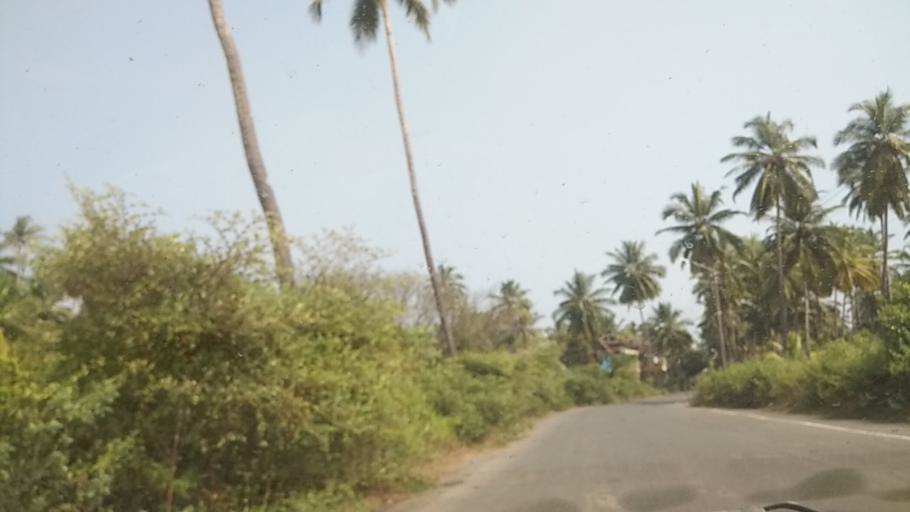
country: IN
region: Goa
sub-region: South Goa
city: Cuncolim
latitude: 15.1653
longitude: 73.9711
